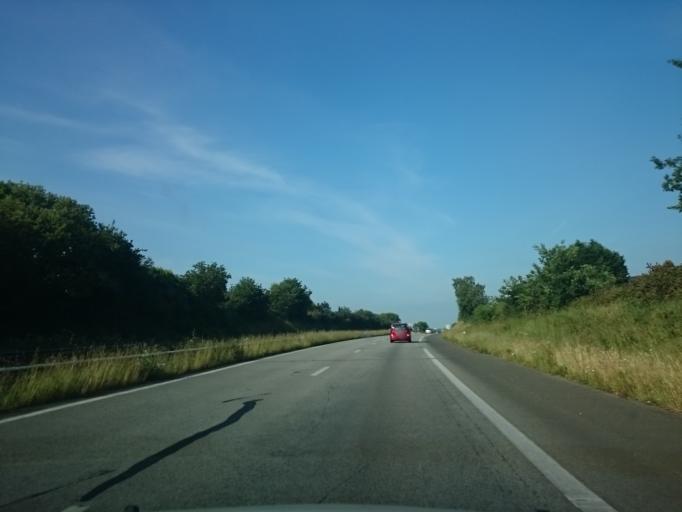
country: FR
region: Brittany
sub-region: Departement du Finistere
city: Quimper
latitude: 48.0405
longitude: -4.0732
